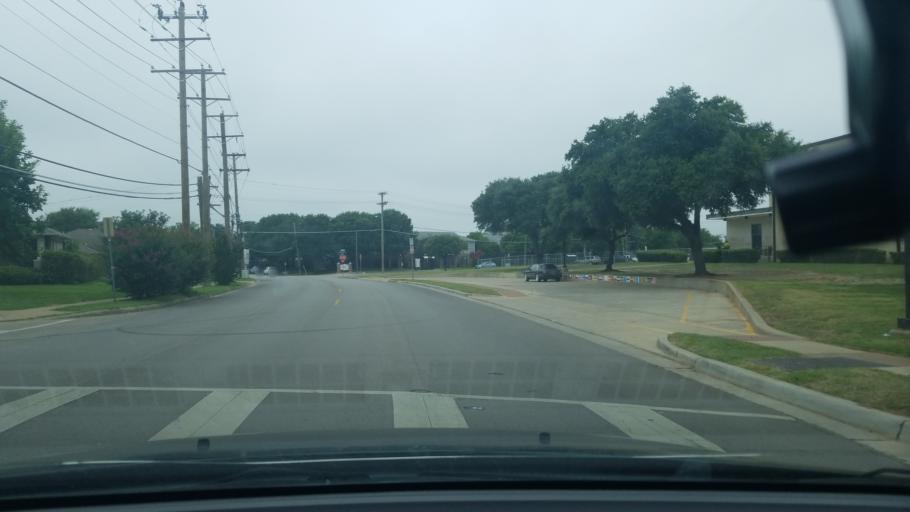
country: US
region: Texas
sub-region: Dallas County
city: Balch Springs
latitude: 32.7577
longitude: -96.6893
